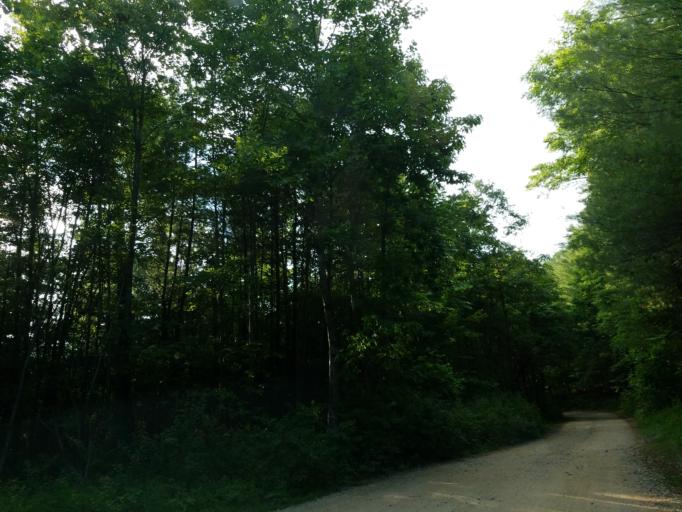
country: US
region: Georgia
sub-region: Fannin County
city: Blue Ridge
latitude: 34.7408
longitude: -84.1749
